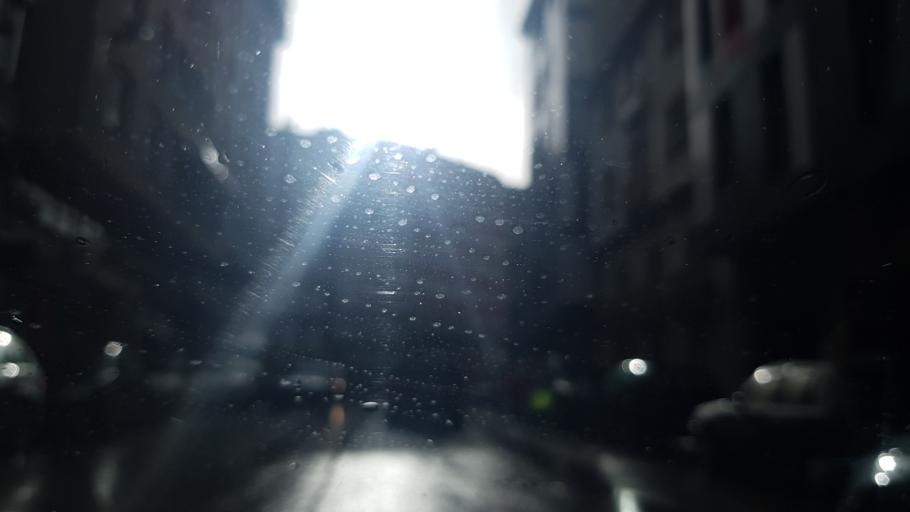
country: ES
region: Galicia
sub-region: Provincia de Lugo
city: Vilalba
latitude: 43.2999
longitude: -7.6788
